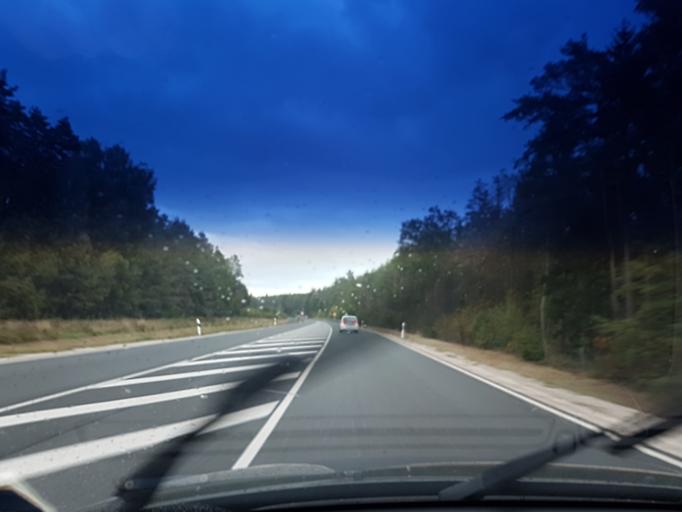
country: DE
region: Bavaria
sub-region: Upper Franconia
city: Pommersfelden
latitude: 49.7557
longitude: 10.8626
